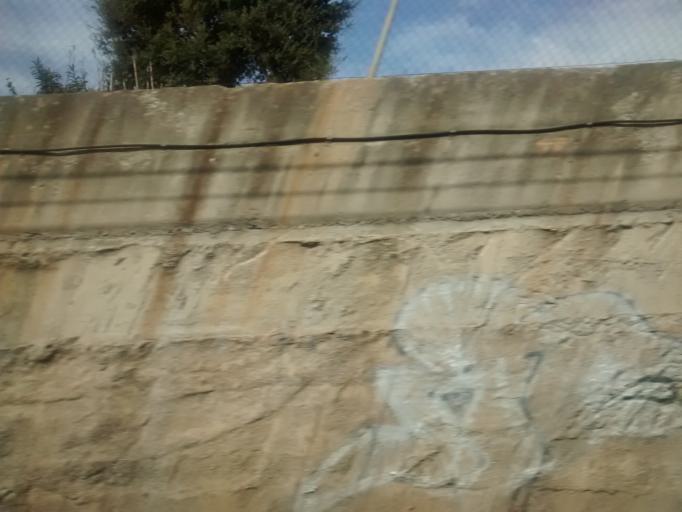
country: ES
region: Catalonia
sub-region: Provincia de Barcelona
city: Sant Joan Despi
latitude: 41.3520
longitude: 2.0607
